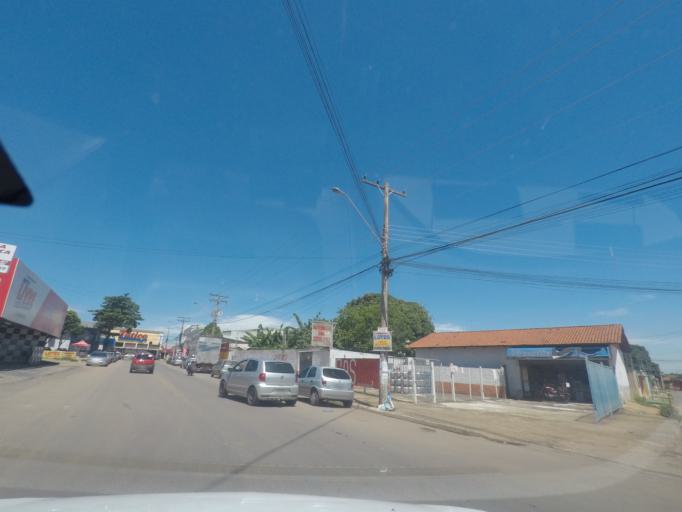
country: BR
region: Goias
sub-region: Aparecida De Goiania
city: Aparecida de Goiania
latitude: -16.7717
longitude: -49.3364
